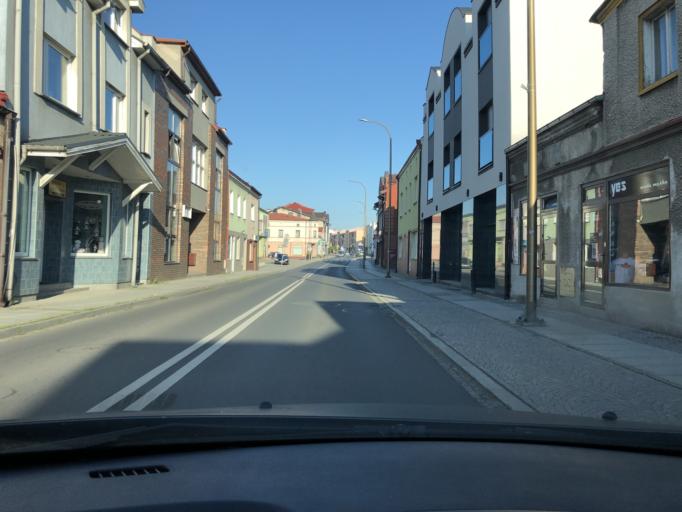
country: PL
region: Lodz Voivodeship
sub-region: Powiat wieruszowski
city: Wieruszow
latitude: 51.2947
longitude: 18.1555
